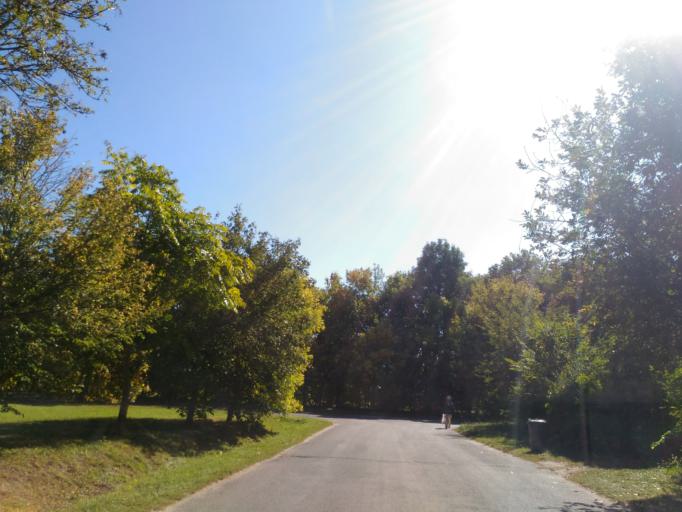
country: HU
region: Fejer
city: Gardony
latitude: 47.1927
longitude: 18.6097
